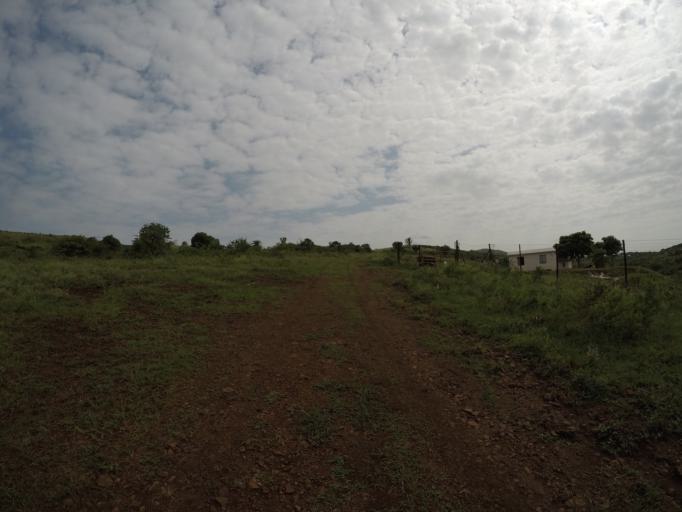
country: ZA
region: KwaZulu-Natal
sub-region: uThungulu District Municipality
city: Empangeni
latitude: -28.6255
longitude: 31.8938
